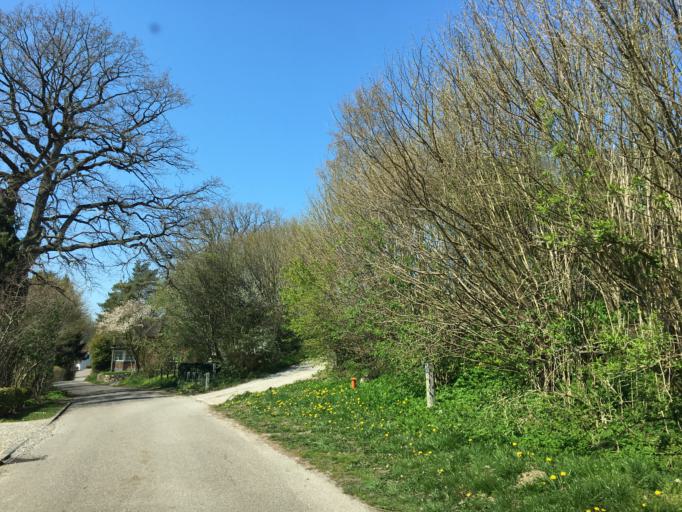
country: DE
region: Schleswig-Holstein
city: Nottfeld
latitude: 54.5938
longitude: 9.8018
